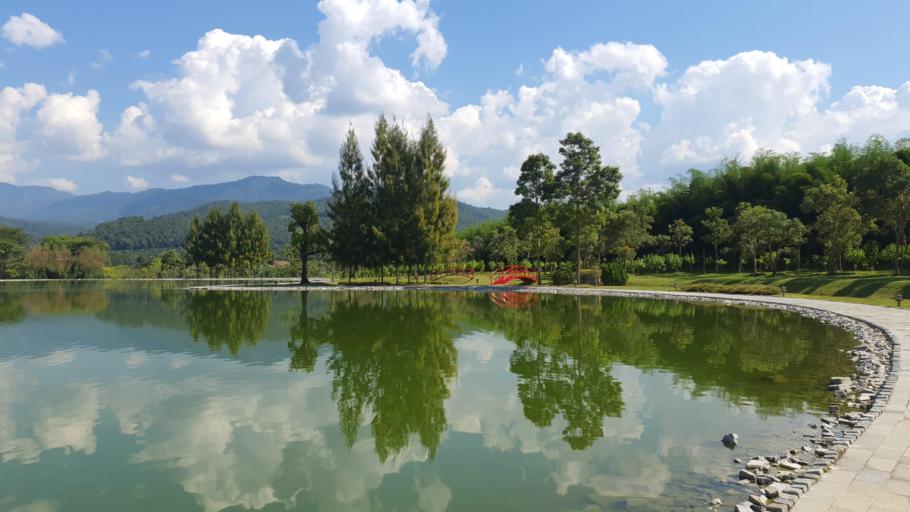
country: TH
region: Chiang Mai
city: Chai Prakan
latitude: 19.6555
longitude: 99.1485
